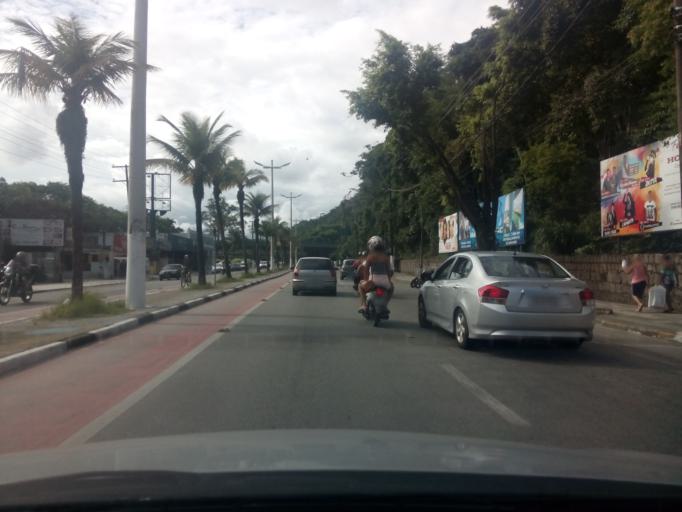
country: BR
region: Sao Paulo
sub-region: Guaruja
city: Guaruja
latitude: -23.9908
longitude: -46.2594
